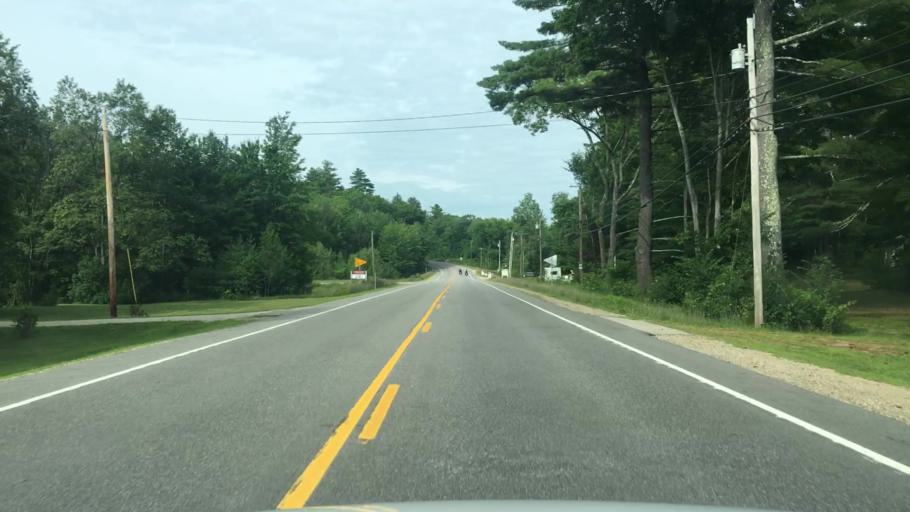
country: US
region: New Hampshire
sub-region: Carroll County
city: Tamworth
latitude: 43.8291
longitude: -71.2923
